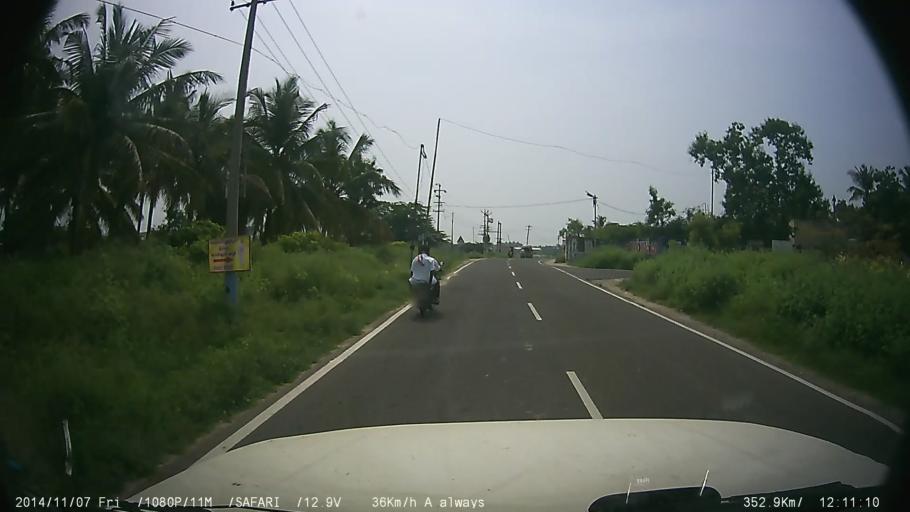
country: IN
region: Tamil Nadu
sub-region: Tiruppur
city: Tiruppur
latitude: 11.1085
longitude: 77.2713
